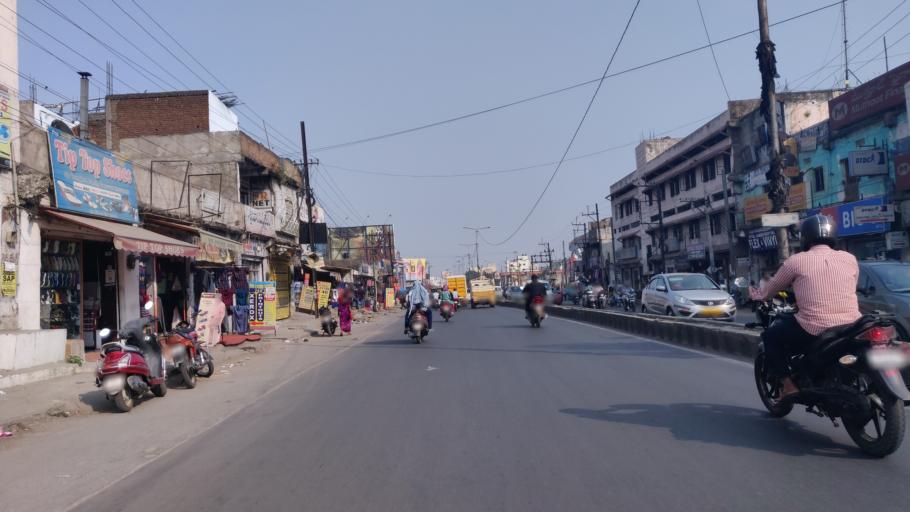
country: IN
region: Telangana
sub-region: Rangareddi
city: Uppal Kalan
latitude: 17.4015
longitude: 78.5670
